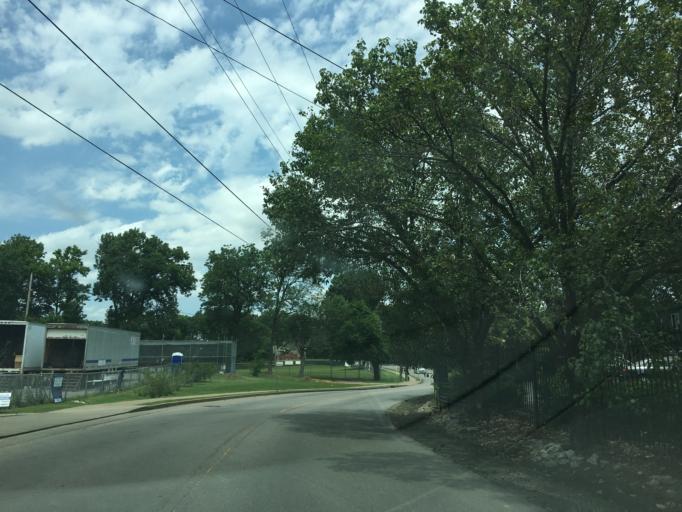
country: US
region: Tennessee
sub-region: Davidson County
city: Oak Hill
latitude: 36.1059
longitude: -86.8085
